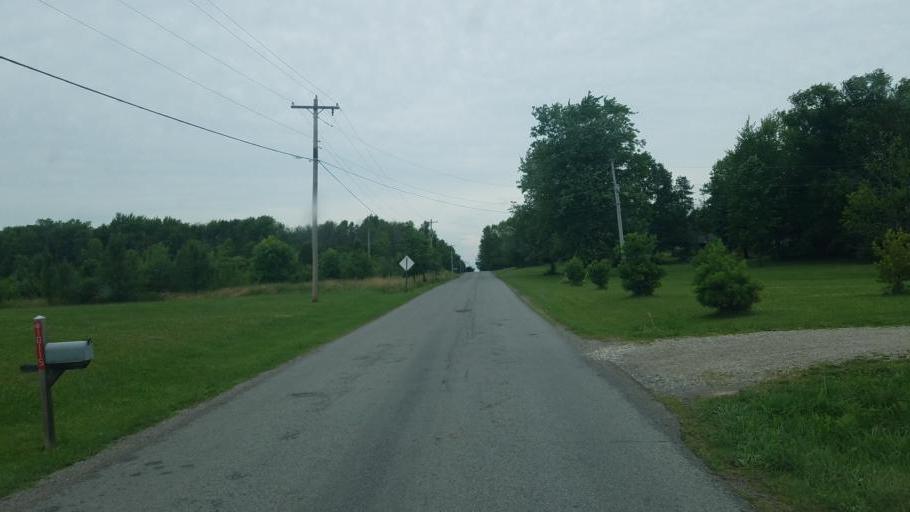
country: US
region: Ohio
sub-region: Licking County
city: Johnstown
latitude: 40.1992
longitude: -82.5897
